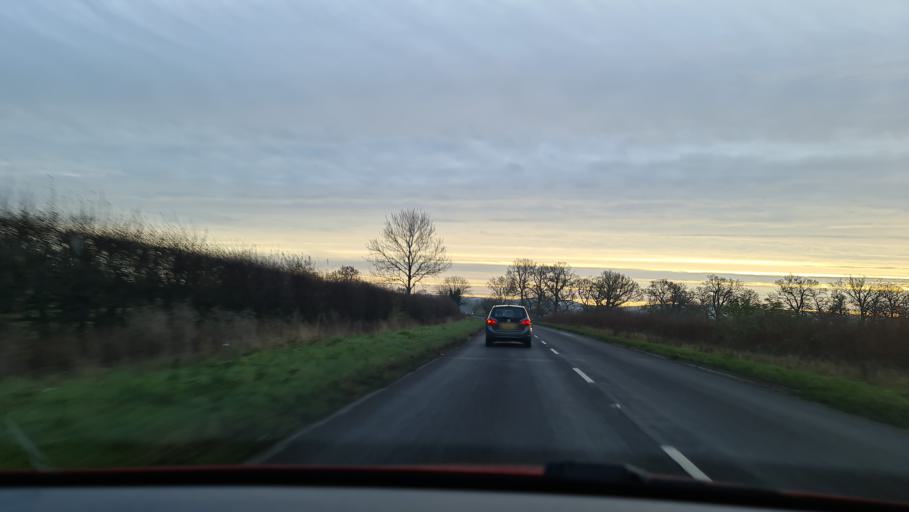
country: GB
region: England
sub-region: Buckinghamshire
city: Haddenham
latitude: 51.7537
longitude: -0.9016
